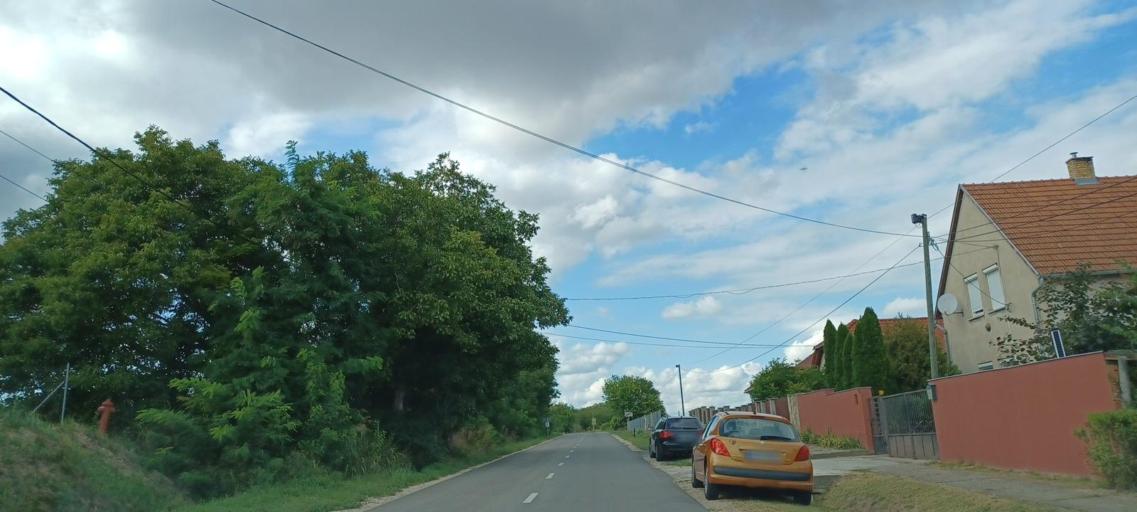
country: HU
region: Tolna
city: Szentgalpuszta
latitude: 46.4057
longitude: 18.6164
